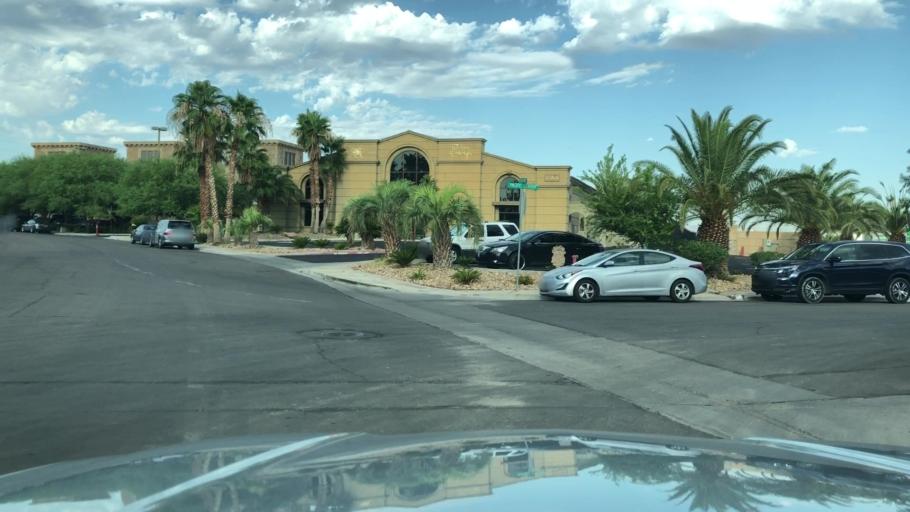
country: US
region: Nevada
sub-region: Clark County
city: Whitney
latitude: 36.0395
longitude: -115.0390
